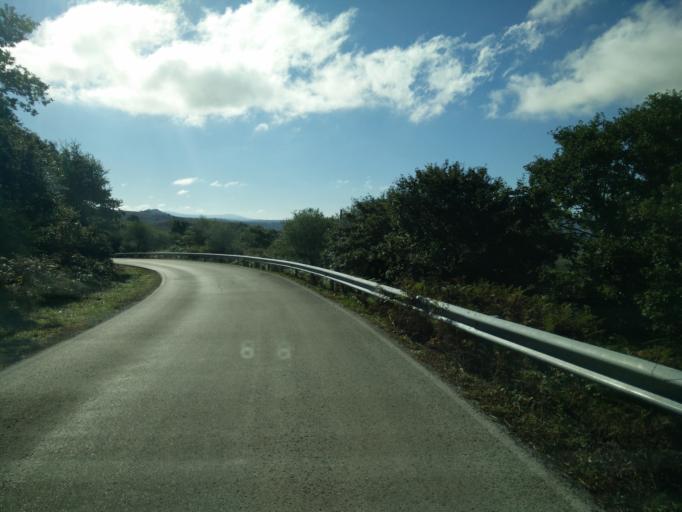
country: ES
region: Castille and Leon
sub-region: Provincia de Burgos
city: Arija
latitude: 43.0329
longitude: -3.8628
